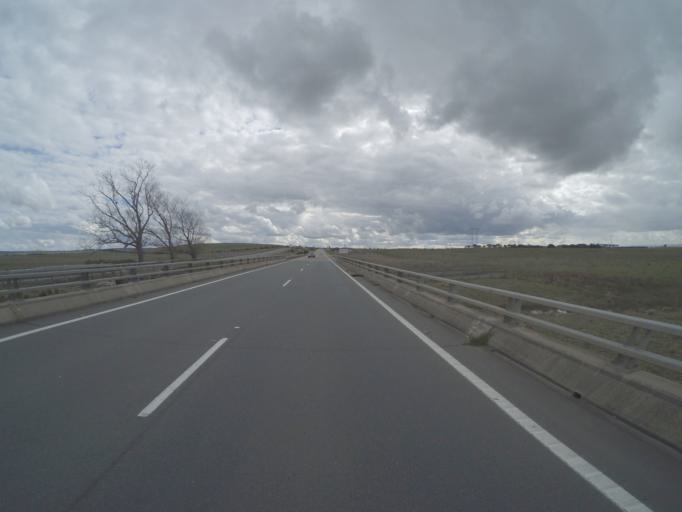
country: AU
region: New South Wales
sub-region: Goulburn Mulwaree
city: Goulburn
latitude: -34.8071
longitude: 149.5492
